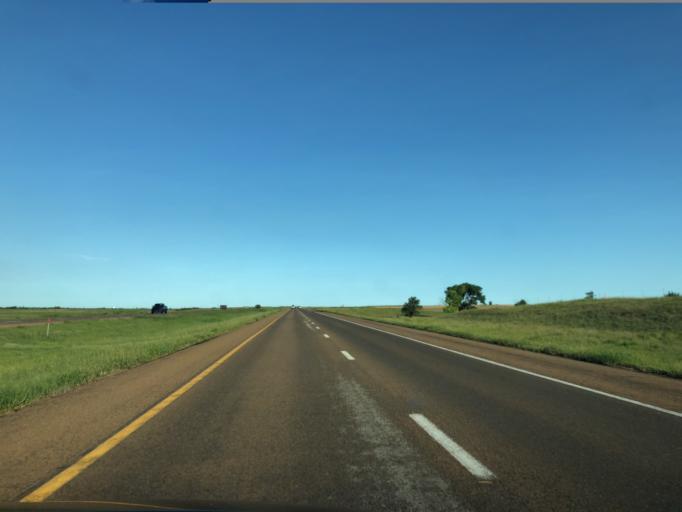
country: US
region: Kansas
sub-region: Ellis County
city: Ellis
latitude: 38.9341
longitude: -99.4677
